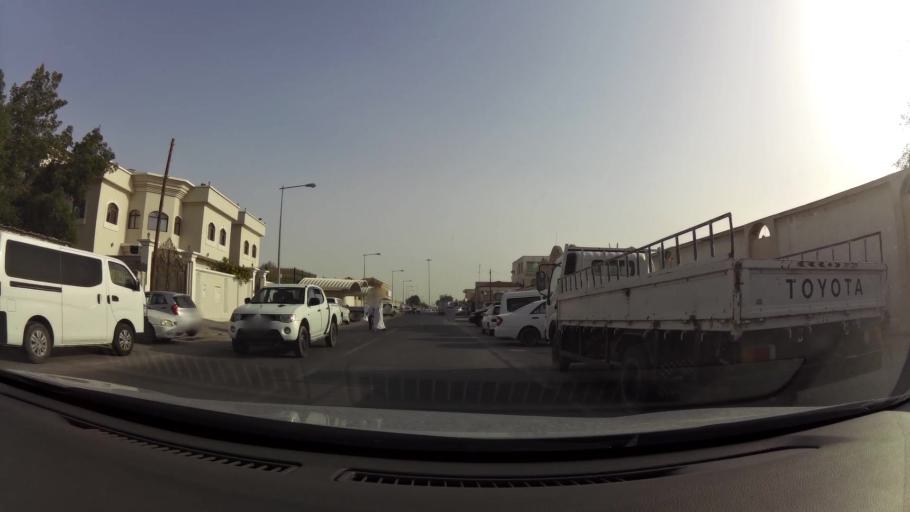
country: QA
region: Baladiyat ar Rayyan
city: Ar Rayyan
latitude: 25.2334
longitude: 51.4367
